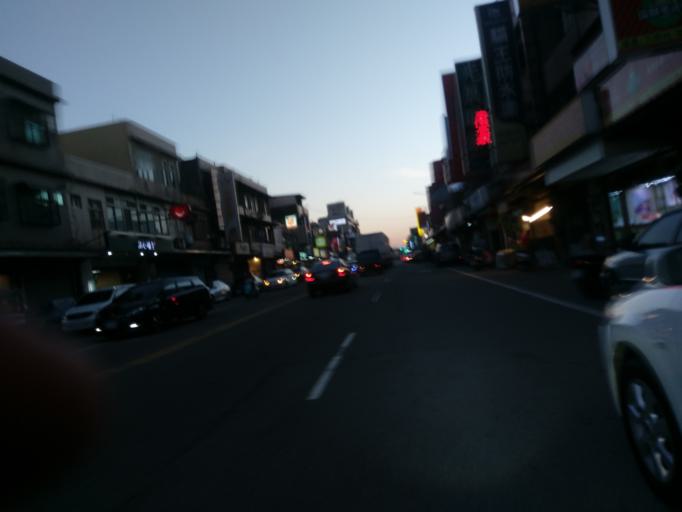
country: TW
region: Taiwan
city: Taoyuan City
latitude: 25.0471
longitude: 121.1424
